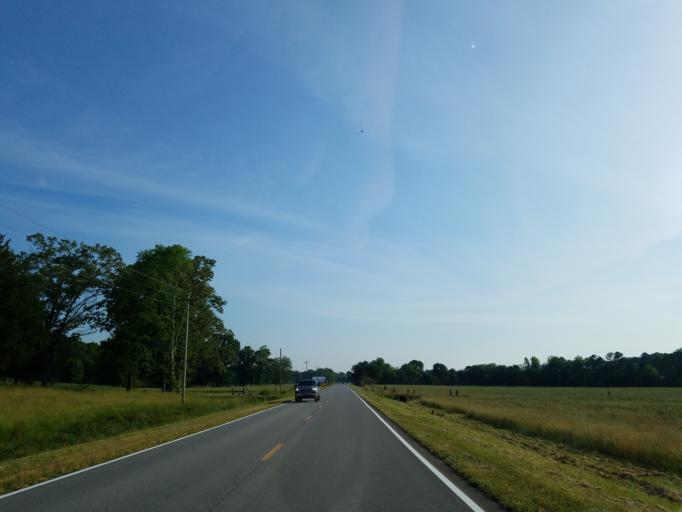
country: US
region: Georgia
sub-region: Chattooga County
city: Trion
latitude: 34.5051
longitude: -85.2413
